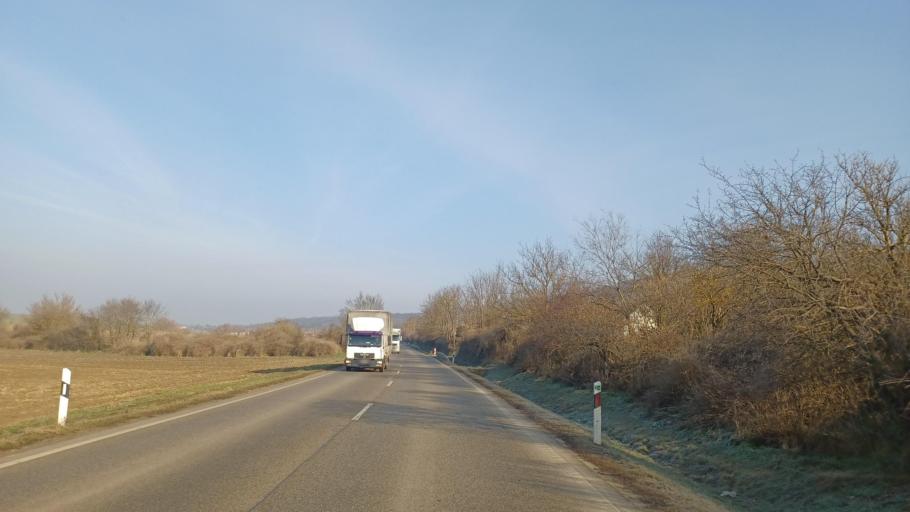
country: HU
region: Tolna
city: Pincehely
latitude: 46.6975
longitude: 18.4645
